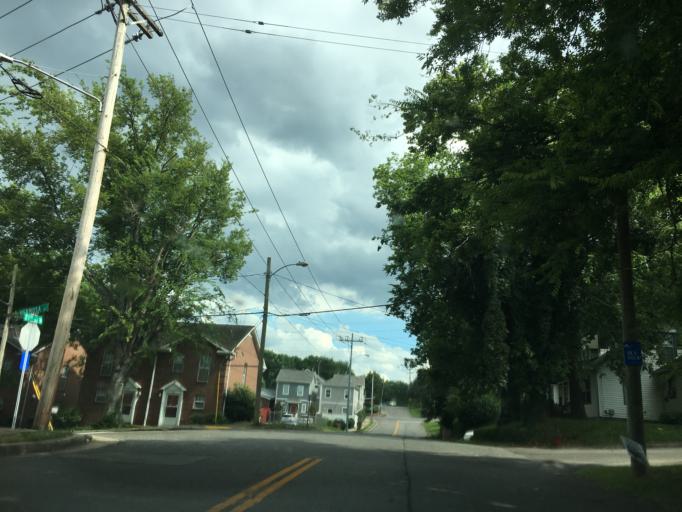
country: US
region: Tennessee
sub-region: Davidson County
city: Nashville
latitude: 36.1639
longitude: -86.8085
